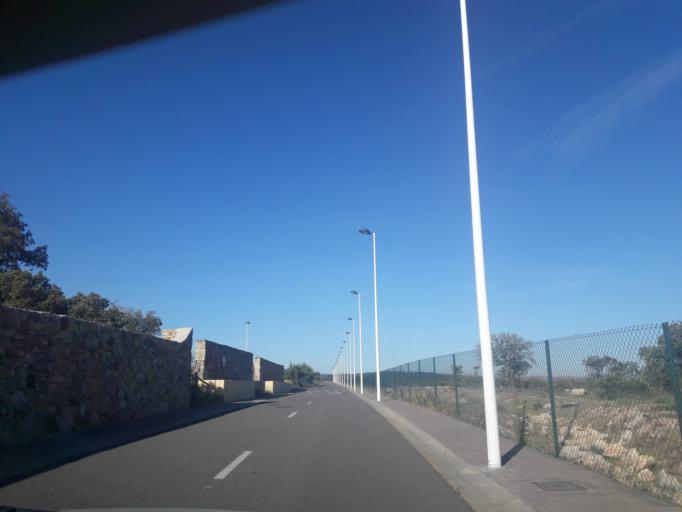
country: ES
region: Castille and Leon
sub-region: Provincia de Salamanca
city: Mozarbez
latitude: 40.8081
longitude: -5.6488
